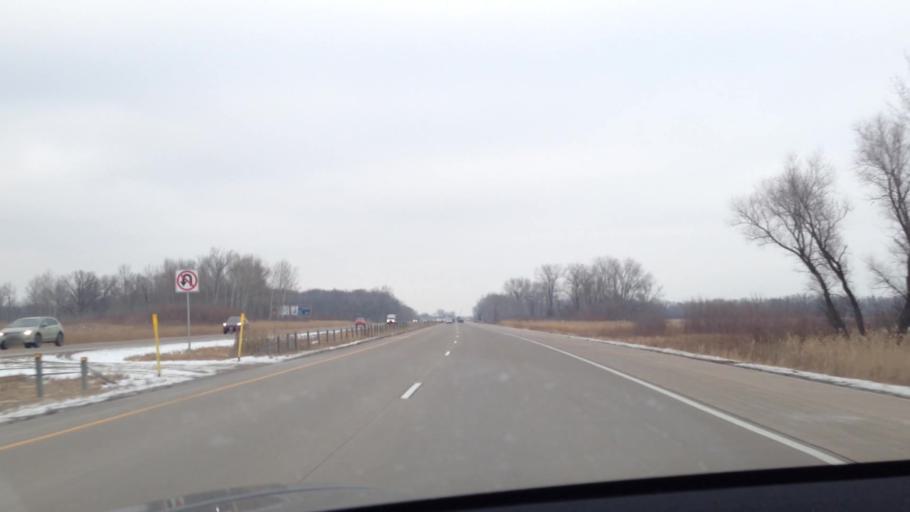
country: US
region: Minnesota
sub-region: Anoka County
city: Centerville
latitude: 45.2003
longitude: -93.0519
